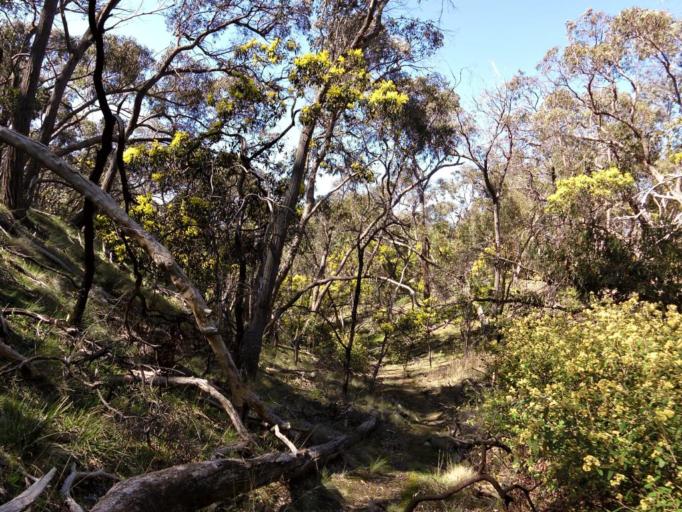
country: AU
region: Victoria
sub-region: Moorabool
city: Bacchus Marsh
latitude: -37.6605
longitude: 144.3211
